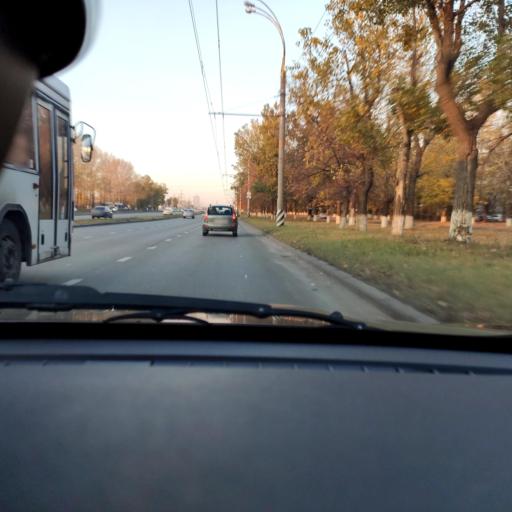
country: RU
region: Samara
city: Tol'yatti
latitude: 53.5261
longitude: 49.2607
